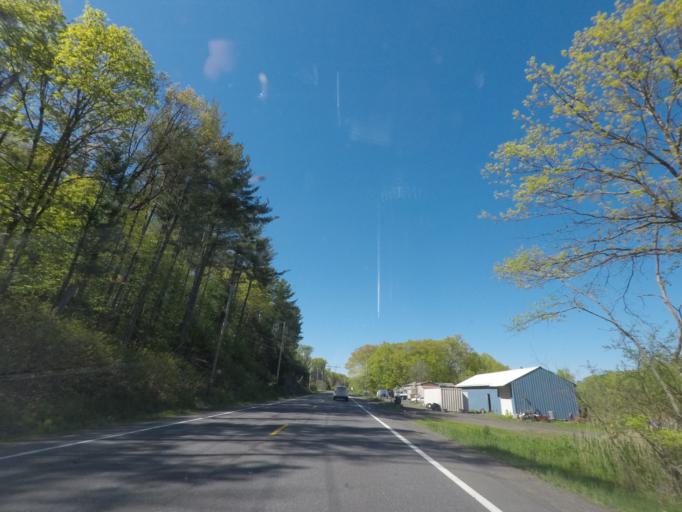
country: US
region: New York
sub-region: Greene County
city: Jefferson Heights
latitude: 42.2623
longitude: -73.8585
